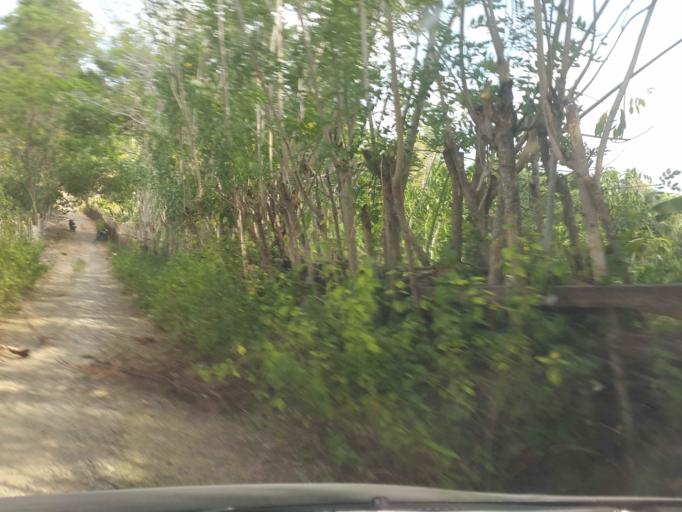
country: ID
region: South Sulawesi
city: Bantaeng
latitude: -6.1727
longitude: 120.4915
